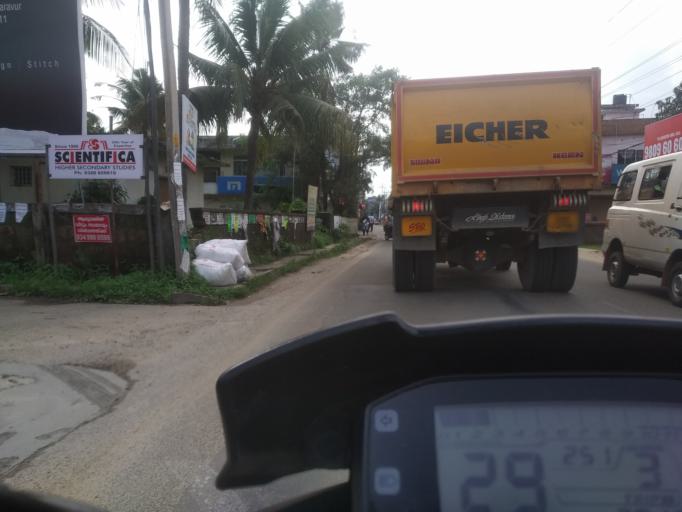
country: IN
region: Kerala
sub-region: Thrissur District
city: Kodungallur
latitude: 10.1433
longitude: 76.2282
